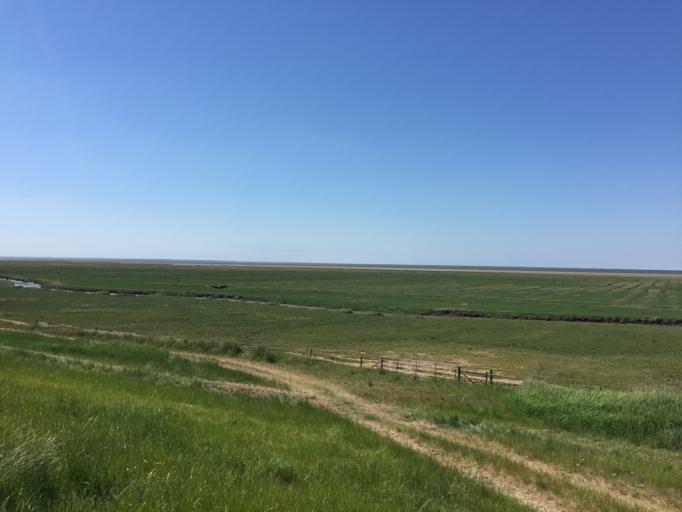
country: DK
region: South Denmark
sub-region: Esbjerg Kommune
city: Ribe
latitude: 55.2517
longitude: 8.6667
